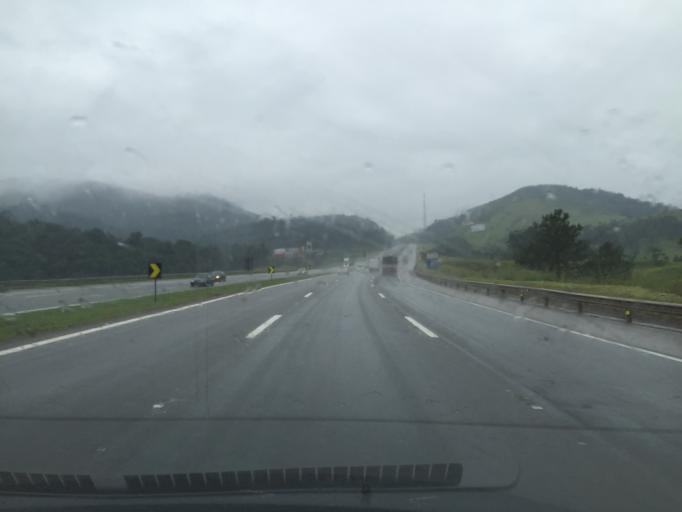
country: BR
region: Sao Paulo
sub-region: Sao Roque
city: Sao Roque
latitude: -23.4298
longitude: -47.1297
